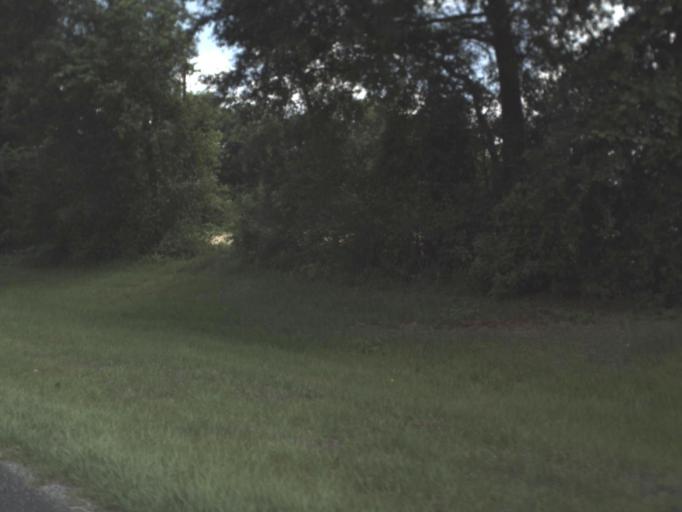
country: US
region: Florida
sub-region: Alachua County
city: High Springs
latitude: 29.8162
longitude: -82.5719
